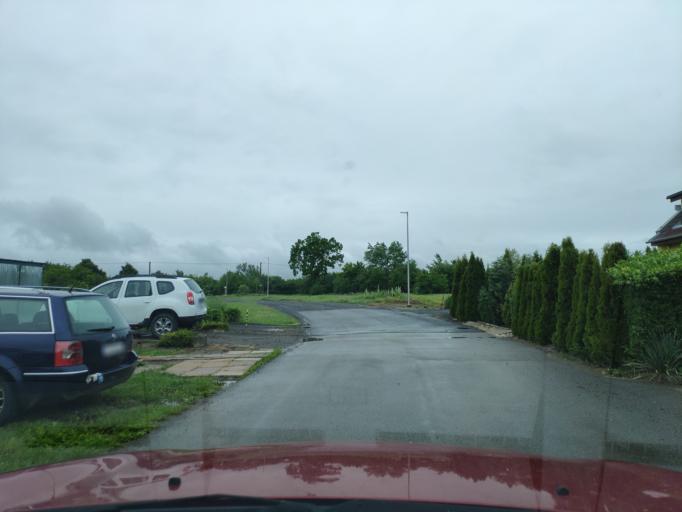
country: SK
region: Kosicky
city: Cierna nad Tisou
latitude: 48.4040
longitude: 22.0620
